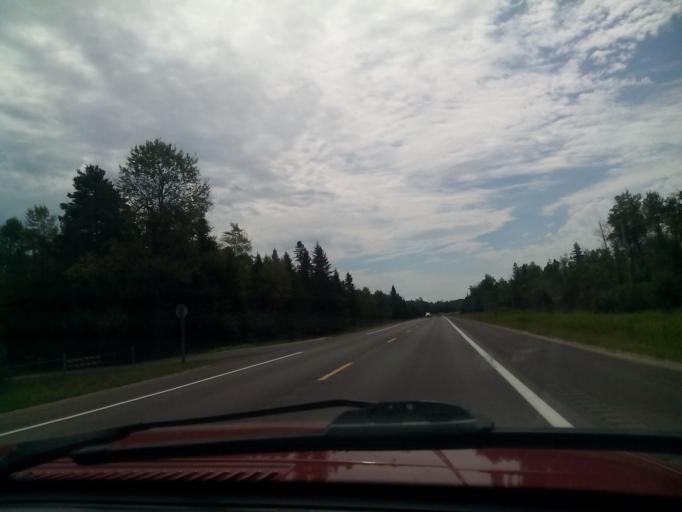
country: US
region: Michigan
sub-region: Schoolcraft County
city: Manistique
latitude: 46.0679
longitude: -85.9584
